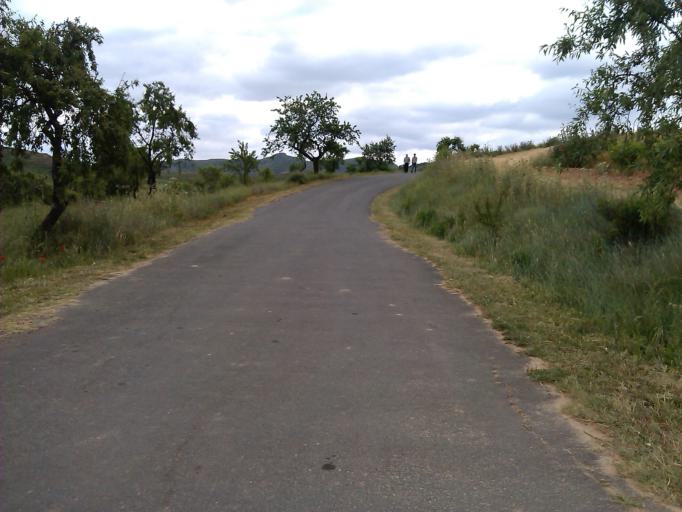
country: ES
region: La Rioja
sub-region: Provincia de La Rioja
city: Navarrete
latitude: 42.4387
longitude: -2.5152
